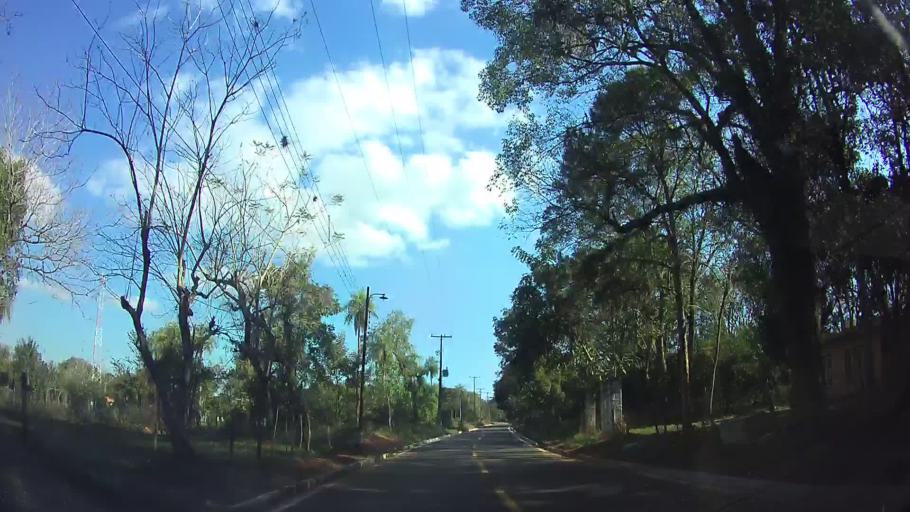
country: PY
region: Central
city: Aregua
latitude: -25.2731
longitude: -57.4392
